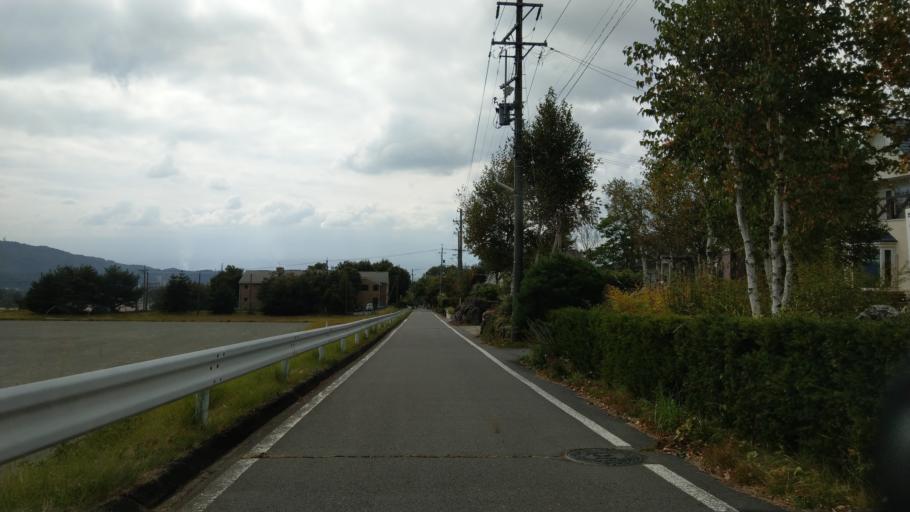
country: JP
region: Nagano
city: Komoro
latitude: 36.3233
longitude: 138.5267
